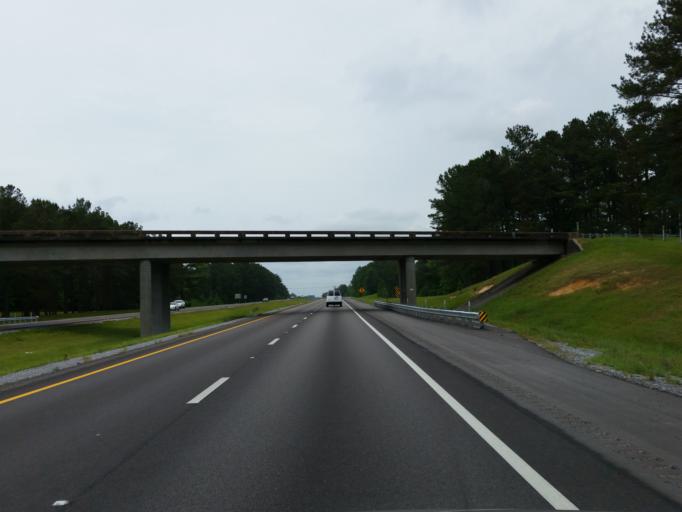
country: US
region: Mississippi
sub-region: Jones County
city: Sharon
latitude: 31.7842
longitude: -89.0553
